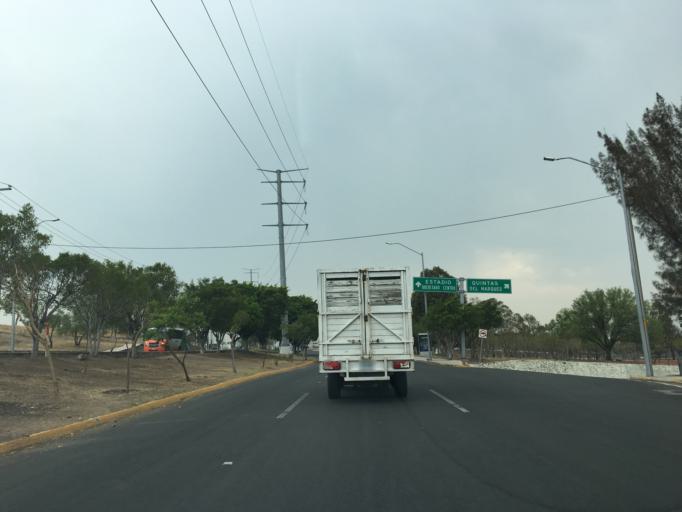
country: MX
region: Queretaro
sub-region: Queretaro
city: Santiago de Queretaro
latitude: 20.5801
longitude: -100.3661
